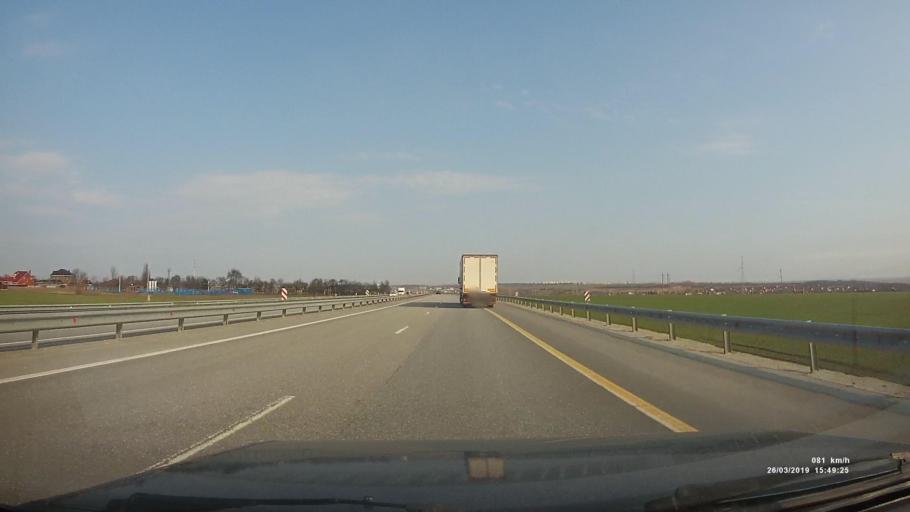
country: RU
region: Rostov
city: Chaltyr
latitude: 47.2760
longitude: 39.4690
